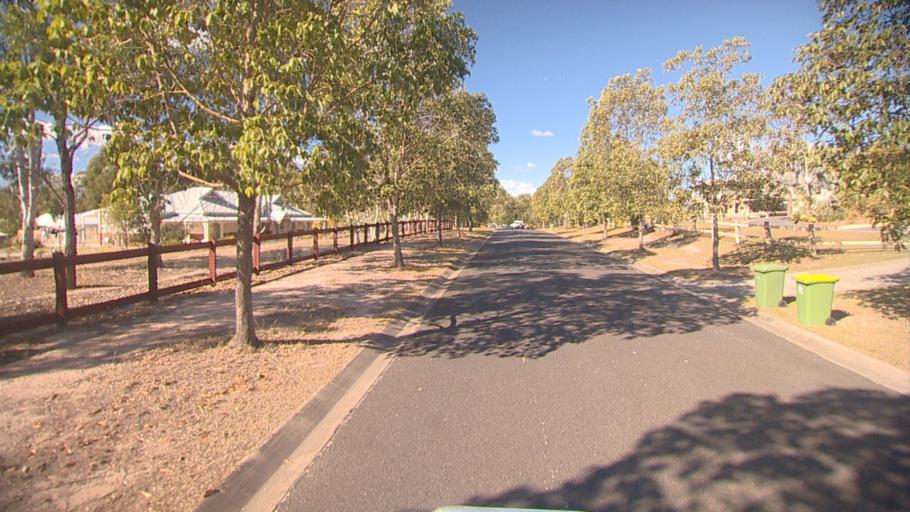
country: AU
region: Queensland
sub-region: Ipswich
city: Springfield Lakes
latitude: -27.7343
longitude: 152.9168
